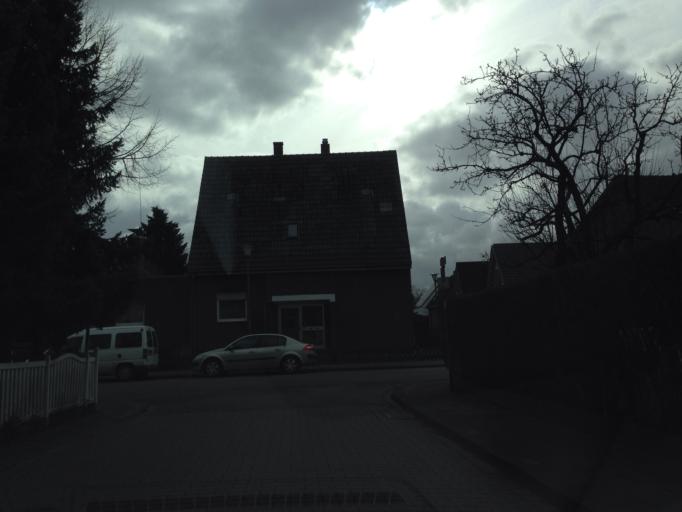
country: DE
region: North Rhine-Westphalia
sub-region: Regierungsbezirk Munster
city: Muenster
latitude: 51.9961
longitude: 7.6115
